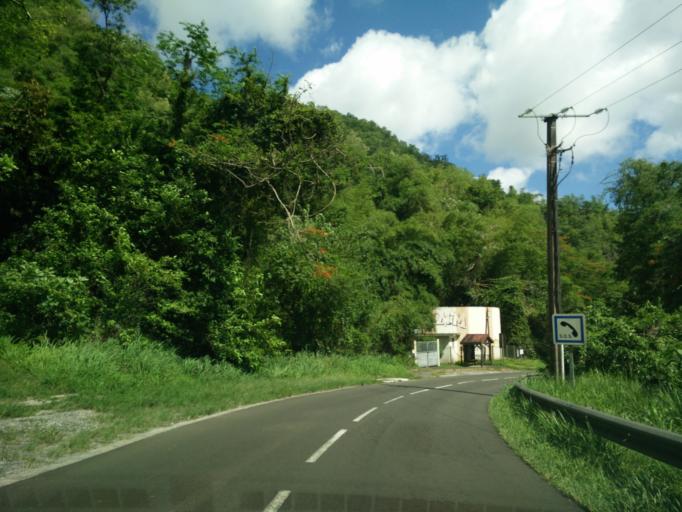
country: MQ
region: Martinique
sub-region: Martinique
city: Les Trois-Ilets
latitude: 14.5151
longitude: -61.0743
